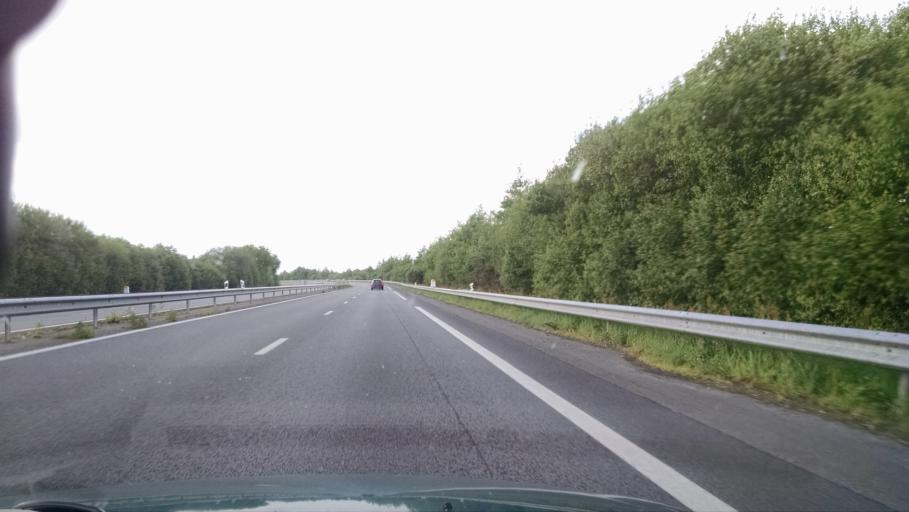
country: FR
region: Brittany
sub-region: Departement du Finistere
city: Taule
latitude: 48.5985
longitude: -3.8879
